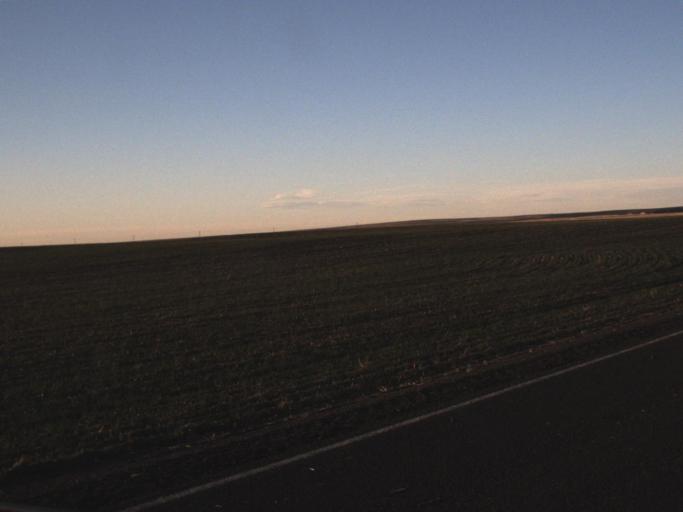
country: US
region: Washington
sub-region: Franklin County
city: Connell
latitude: 46.8170
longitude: -118.5472
